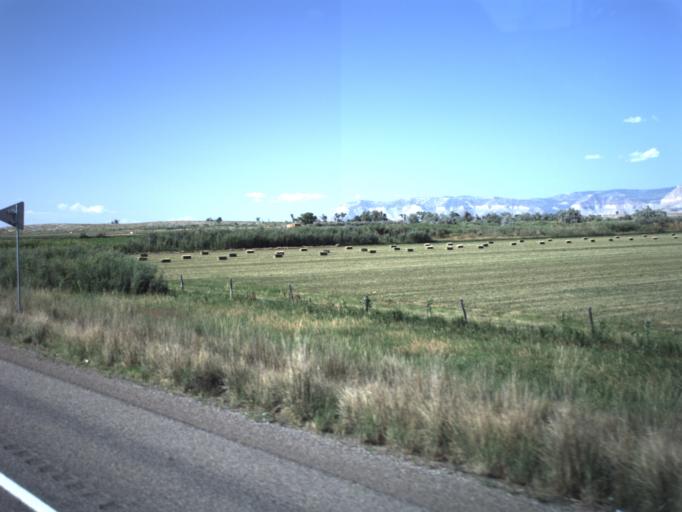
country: US
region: Utah
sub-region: Emery County
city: Castle Dale
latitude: 39.2071
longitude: -111.0243
